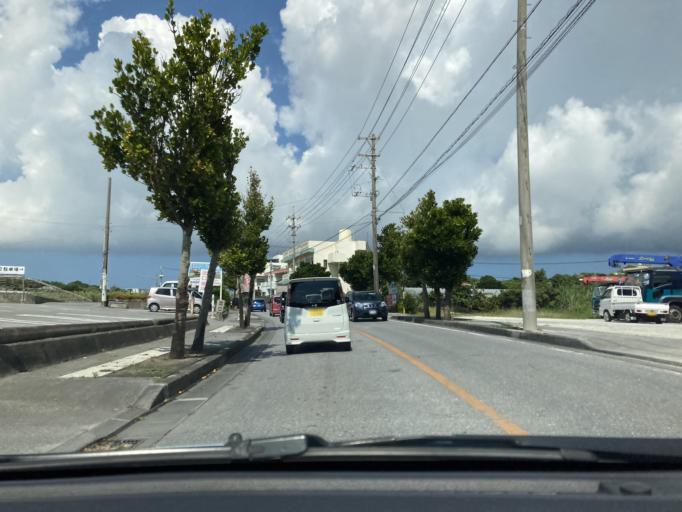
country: JP
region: Okinawa
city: Tomigusuku
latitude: 26.1713
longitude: 127.7372
